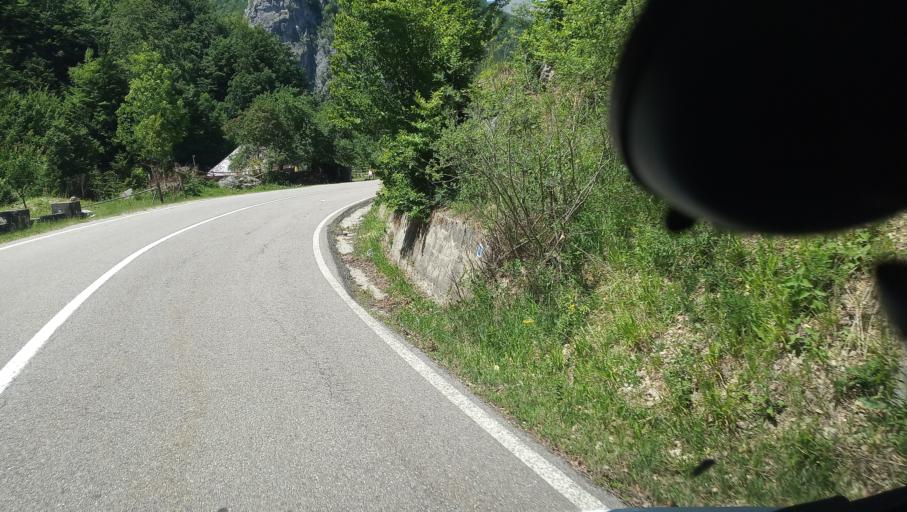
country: RO
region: Mehedinti
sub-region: Comuna Isverna
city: Isverna
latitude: 45.0543
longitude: 22.6061
